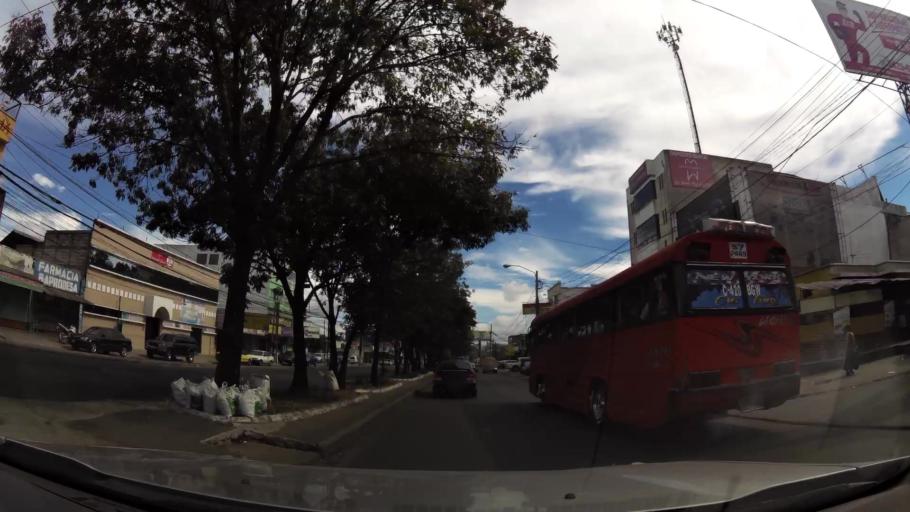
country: GT
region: Guatemala
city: Mixco
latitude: 14.6440
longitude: -90.5743
